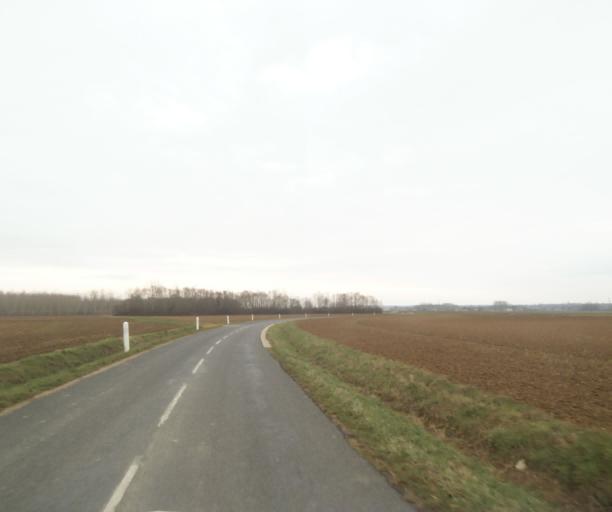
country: FR
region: Champagne-Ardenne
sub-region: Departement de la Haute-Marne
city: Villiers-en-Lieu
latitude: 48.6319
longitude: 4.7719
